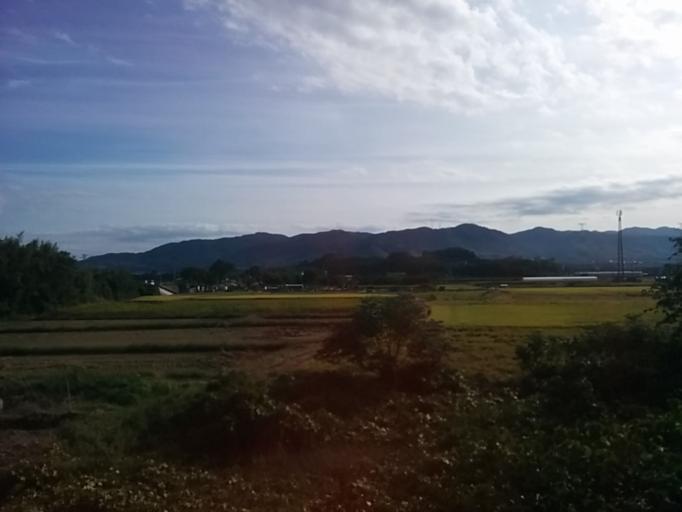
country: JP
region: Kyoto
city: Tanabe
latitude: 34.8048
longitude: 135.7815
